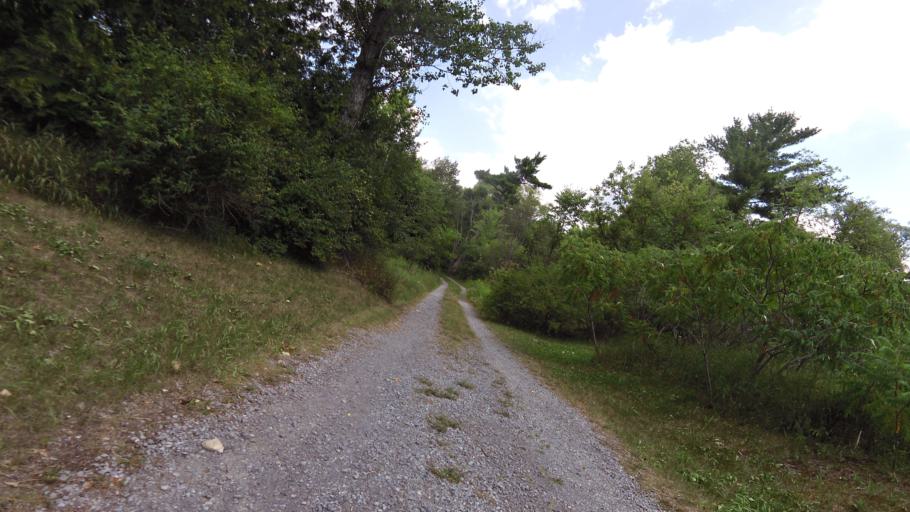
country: CA
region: Ontario
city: Carleton Place
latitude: 45.2677
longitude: -76.2506
